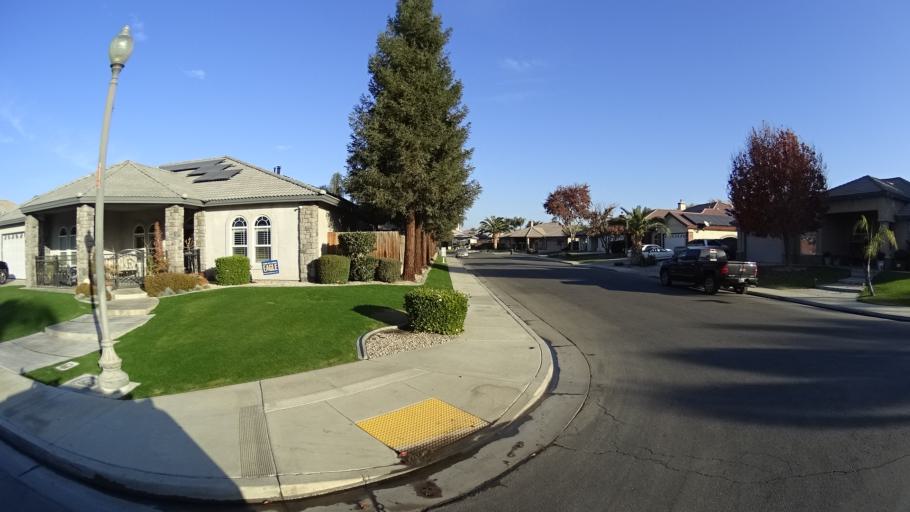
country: US
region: California
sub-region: Kern County
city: Greenfield
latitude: 35.2711
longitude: -119.0519
